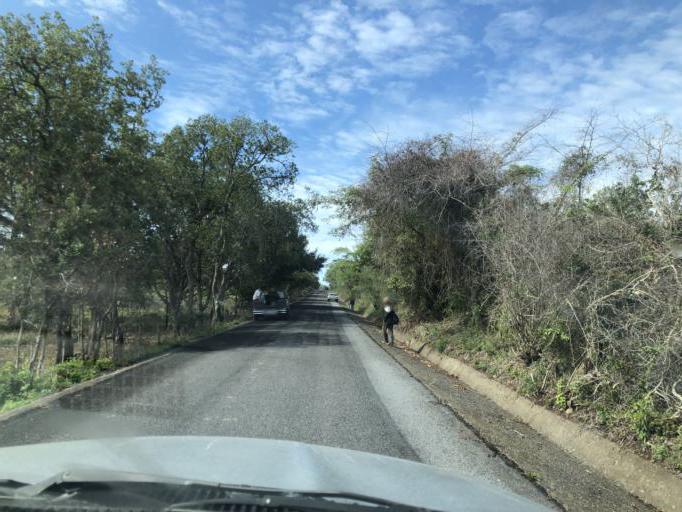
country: MX
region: Veracruz
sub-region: Alto Lucero de Gutierrez Barrios
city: Palma Sola
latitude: 19.7974
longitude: -96.5469
